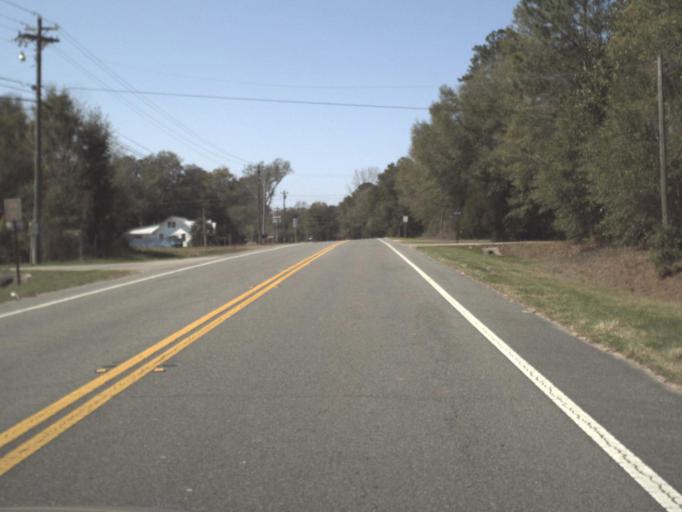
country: US
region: Florida
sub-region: Gadsden County
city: Havana
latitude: 30.6080
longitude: -84.4715
